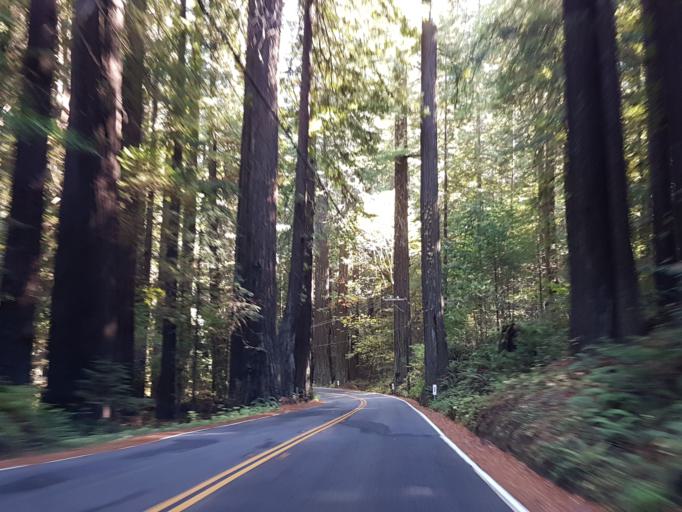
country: US
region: California
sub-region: Humboldt County
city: Rio Dell
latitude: 40.4181
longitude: -123.9764
